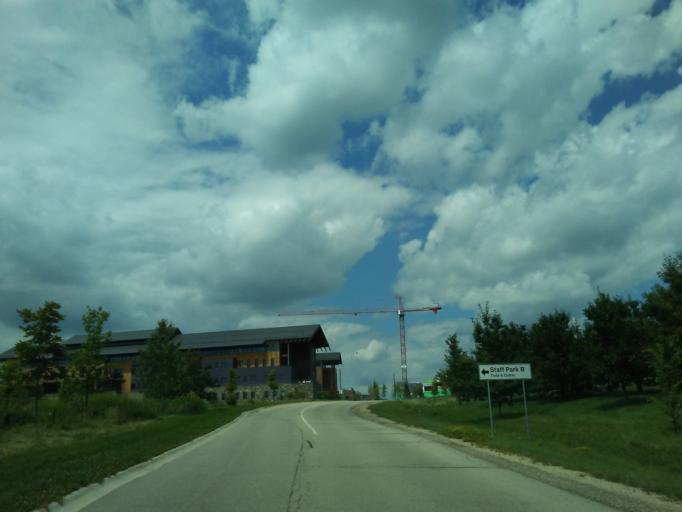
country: US
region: Wisconsin
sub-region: Dane County
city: Verona
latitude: 42.9945
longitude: -89.5633
